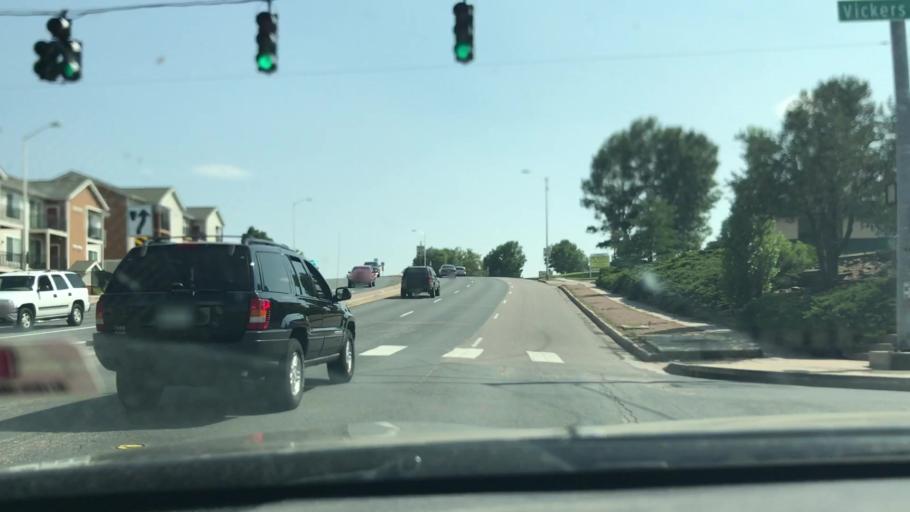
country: US
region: Colorado
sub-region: El Paso County
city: Colorado Springs
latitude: 38.9140
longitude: -104.7754
